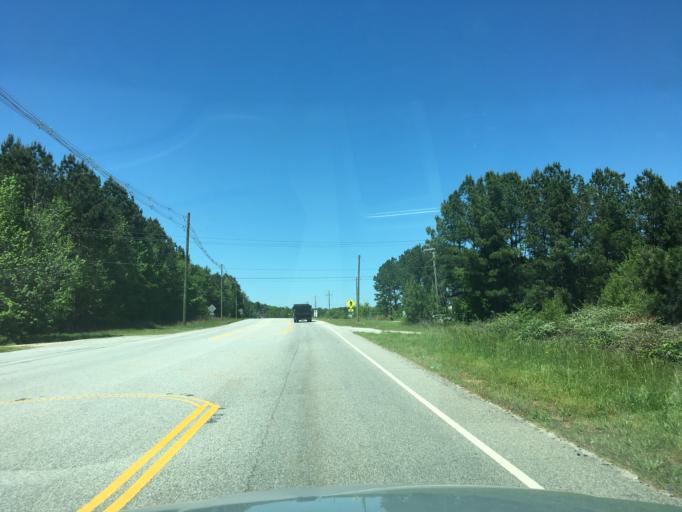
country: US
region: South Carolina
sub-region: Greenville County
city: Greer
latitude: 34.8866
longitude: -82.1956
